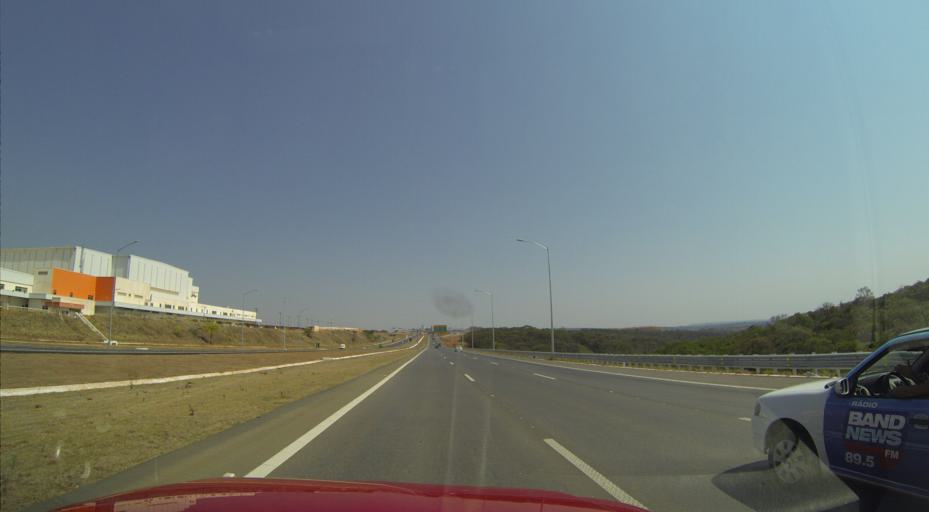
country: BR
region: Minas Gerais
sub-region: Lagoa Santa
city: Lagoa Santa
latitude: -19.6446
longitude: -43.9510
